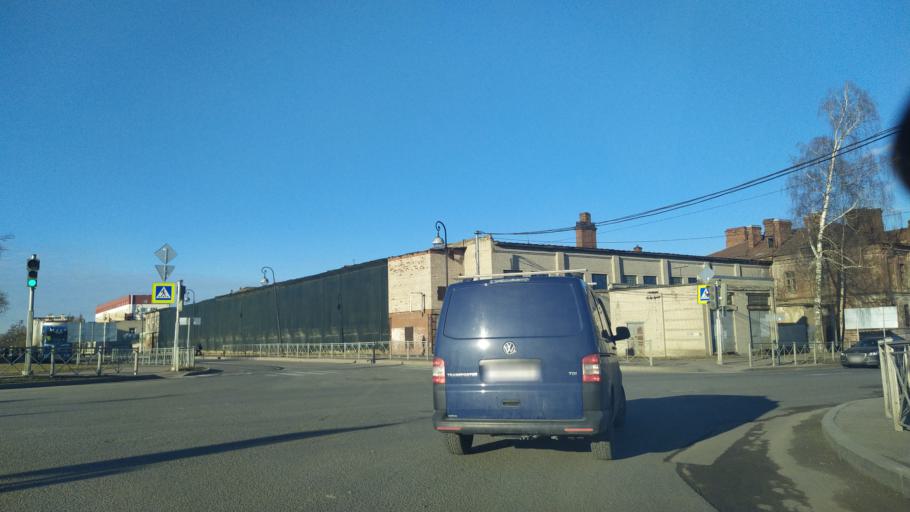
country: RU
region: St.-Petersburg
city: Pushkin
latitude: 59.7006
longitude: 30.3944
